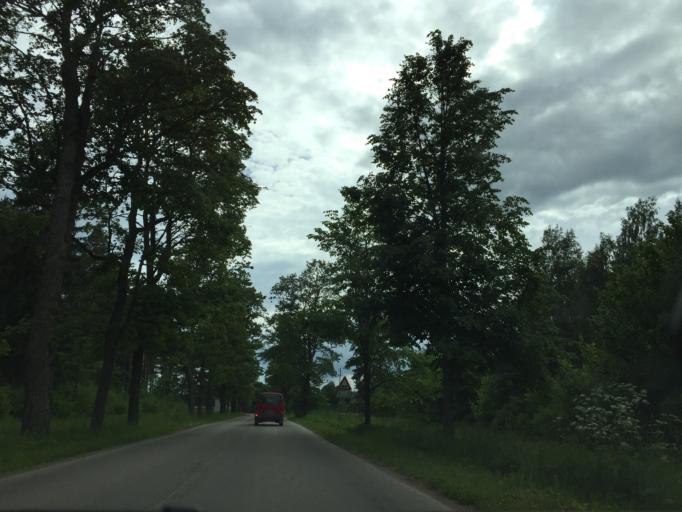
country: LV
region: Apes Novads
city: Ape
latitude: 57.5097
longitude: 26.4018
